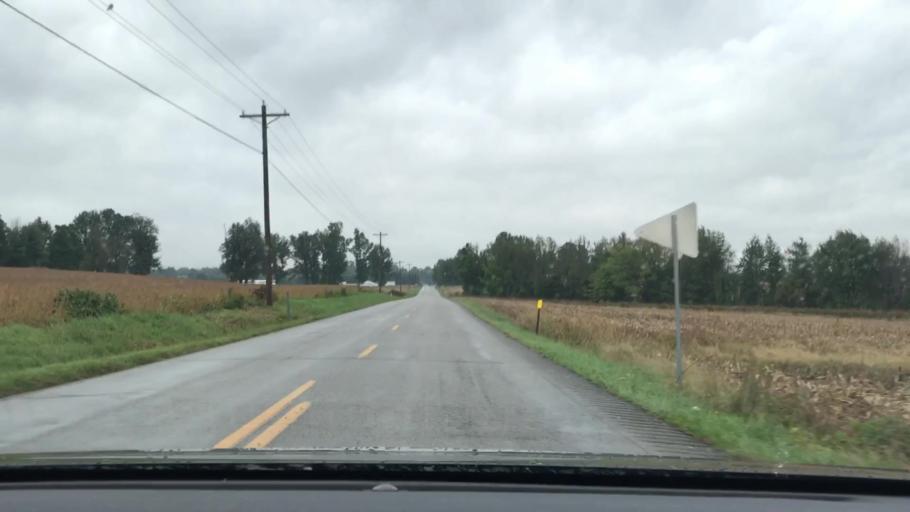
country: US
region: Kentucky
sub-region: McLean County
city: Calhoun
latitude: 37.4299
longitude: -87.2527
